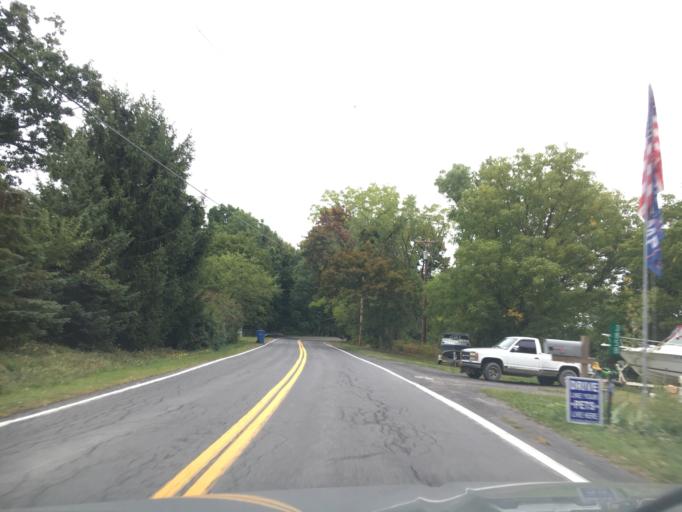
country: US
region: New York
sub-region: Tompkins County
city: Trumansburg
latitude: 42.6610
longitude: -76.7095
